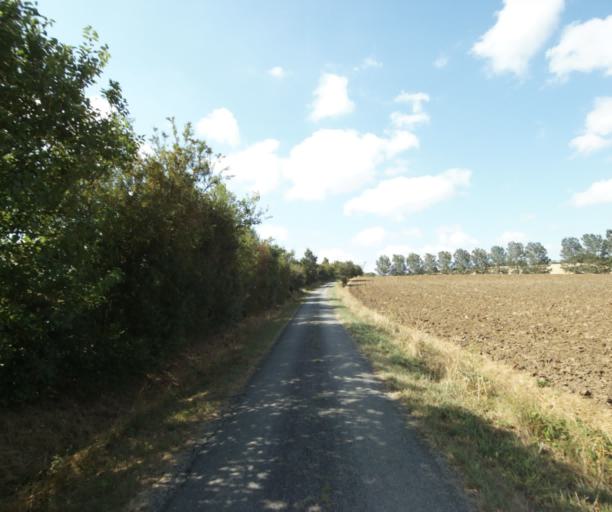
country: FR
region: Midi-Pyrenees
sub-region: Departement de la Haute-Garonne
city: Avignonet-Lauragais
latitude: 43.4389
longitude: 1.7950
